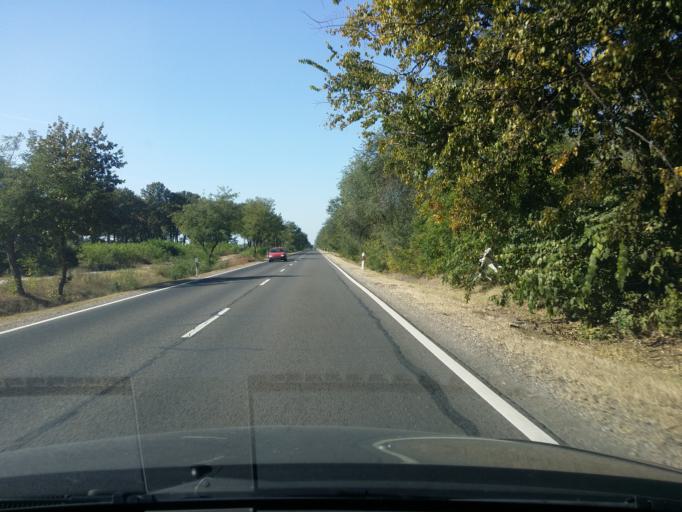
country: HU
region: Bacs-Kiskun
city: Nyarlorinc
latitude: 46.8645
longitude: 19.9119
